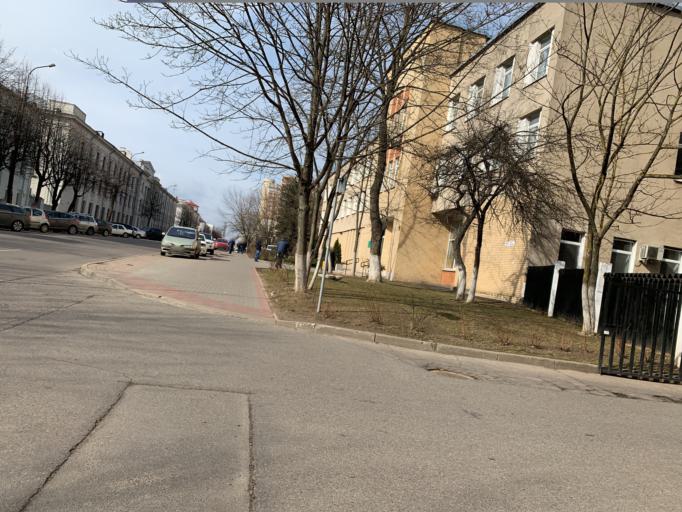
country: BY
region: Minsk
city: Minsk
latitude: 53.9141
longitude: 27.6000
